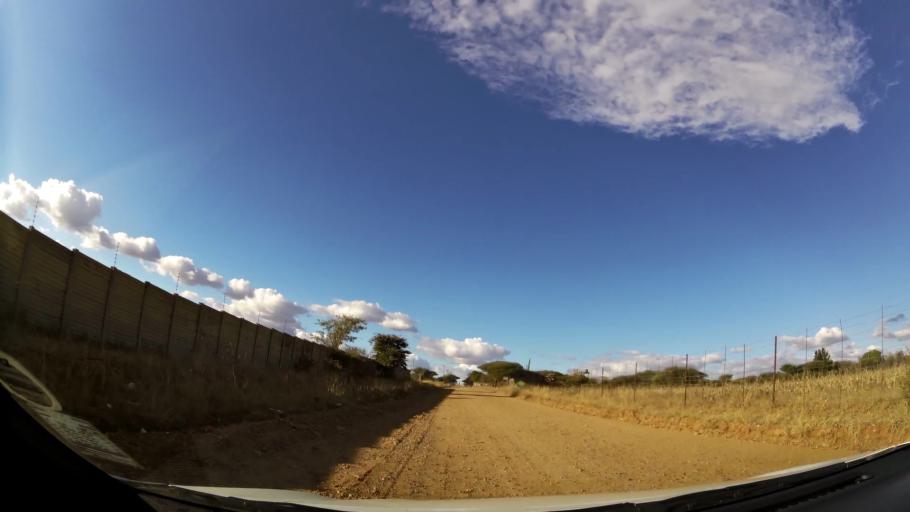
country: ZA
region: Limpopo
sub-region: Capricorn District Municipality
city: Polokwane
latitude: -23.9309
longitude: 29.4327
